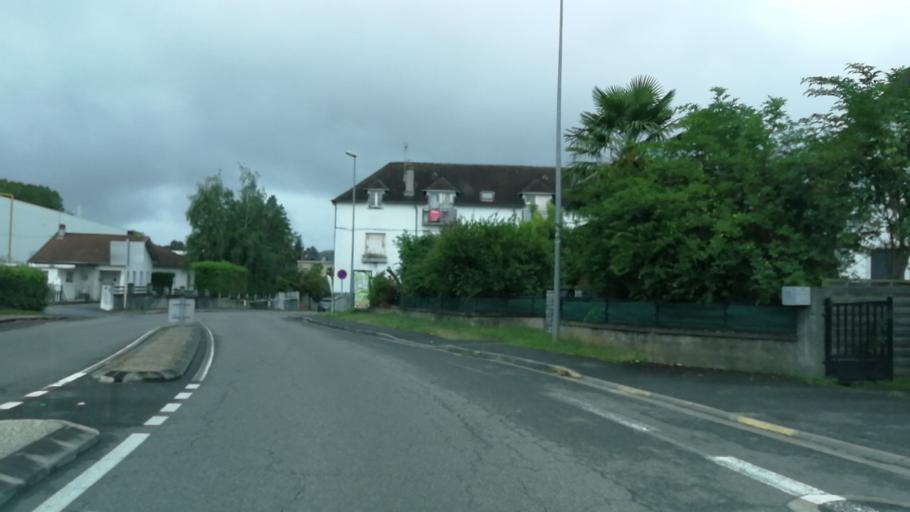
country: FR
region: Aquitaine
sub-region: Departement des Pyrenees-Atlantiques
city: Oloron-Sainte-Marie
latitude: 43.1787
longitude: -0.6064
